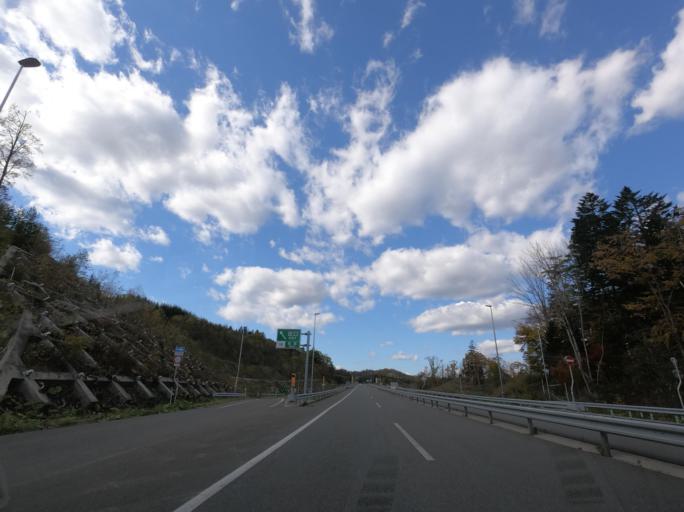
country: JP
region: Hokkaido
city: Kushiro
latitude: 43.0767
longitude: 144.0658
